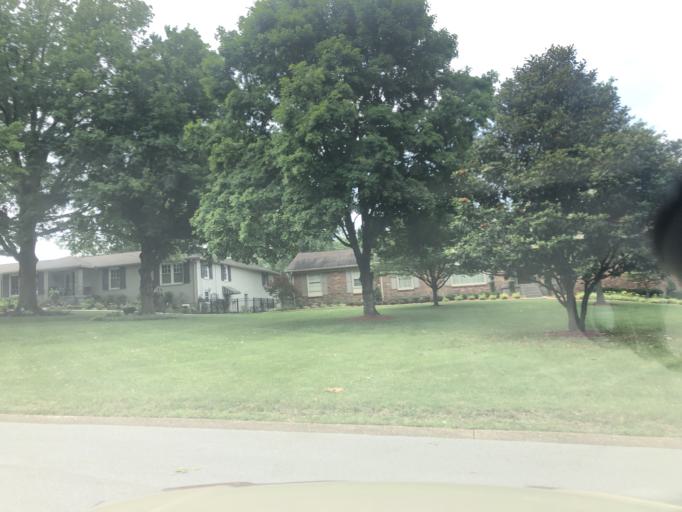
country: US
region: Tennessee
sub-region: Davidson County
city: Lakewood
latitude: 36.2396
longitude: -86.6188
